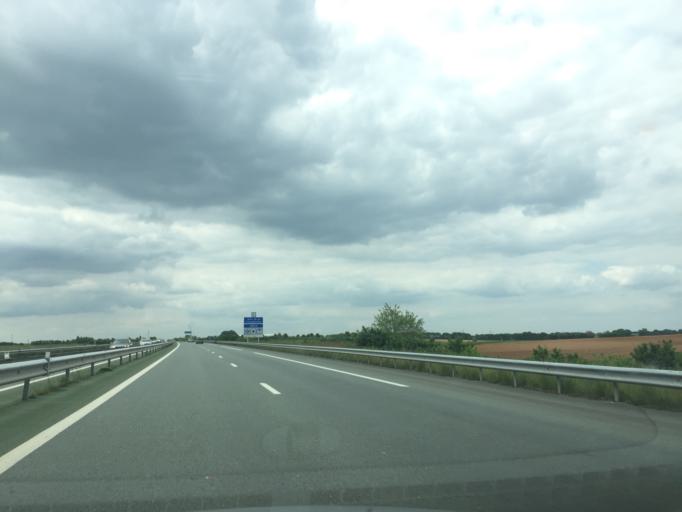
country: FR
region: Poitou-Charentes
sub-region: Departement des Deux-Sevres
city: Saint-Maxire
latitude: 46.4299
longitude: -0.4921
